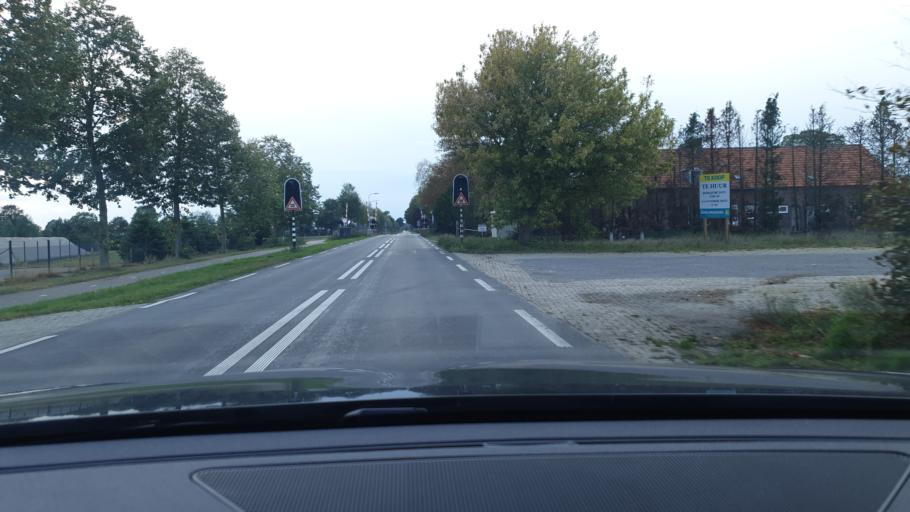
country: NL
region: Limburg
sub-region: Gemeente Venlo
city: Arcen
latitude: 51.4561
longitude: 6.1178
